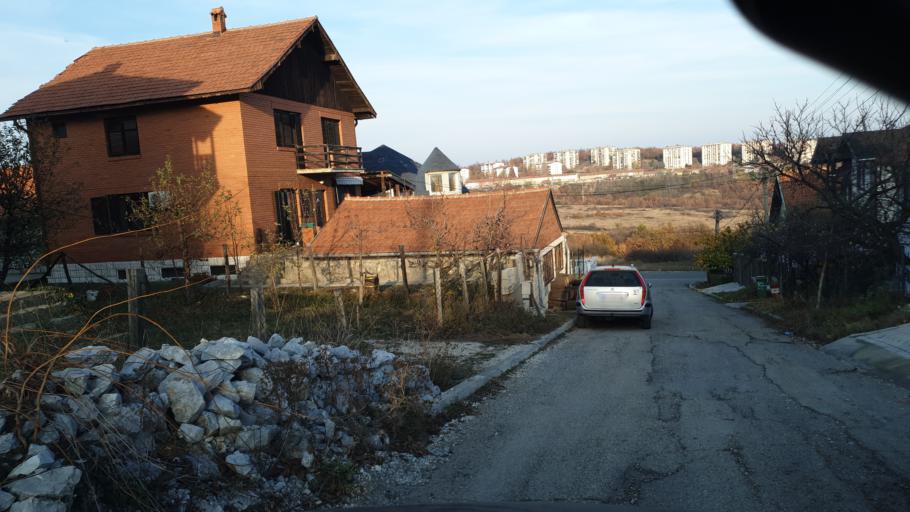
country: RS
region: Central Serbia
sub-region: Borski Okrug
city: Bor
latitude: 44.0538
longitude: 22.0866
